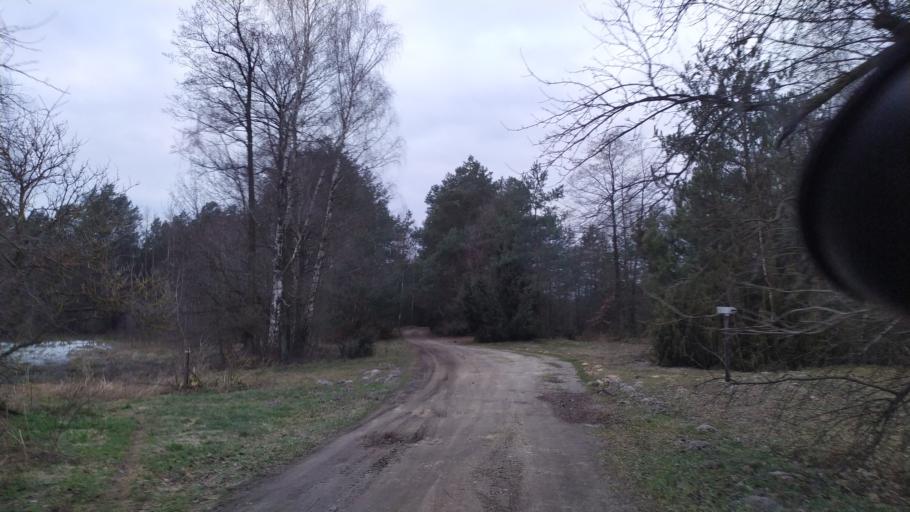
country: PL
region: Lublin Voivodeship
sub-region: Powiat lubartowski
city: Abramow
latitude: 51.4232
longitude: 22.2941
